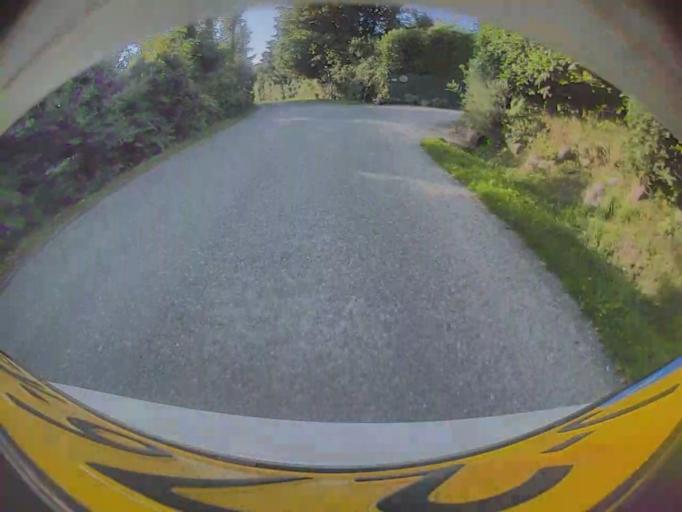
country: IE
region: Leinster
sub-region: Wicklow
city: Enniskerry
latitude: 53.1881
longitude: -6.2320
